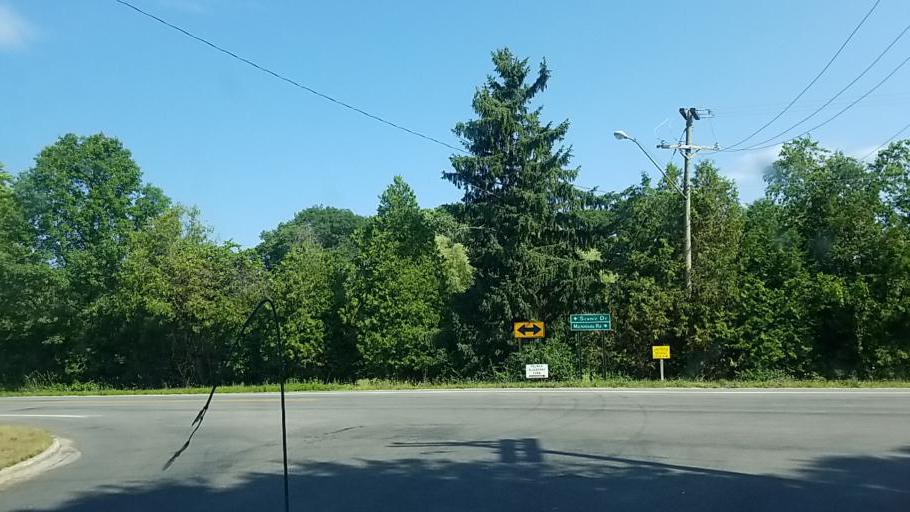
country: US
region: Michigan
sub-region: Muskegon County
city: Montague
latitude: 43.3572
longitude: -86.4105
